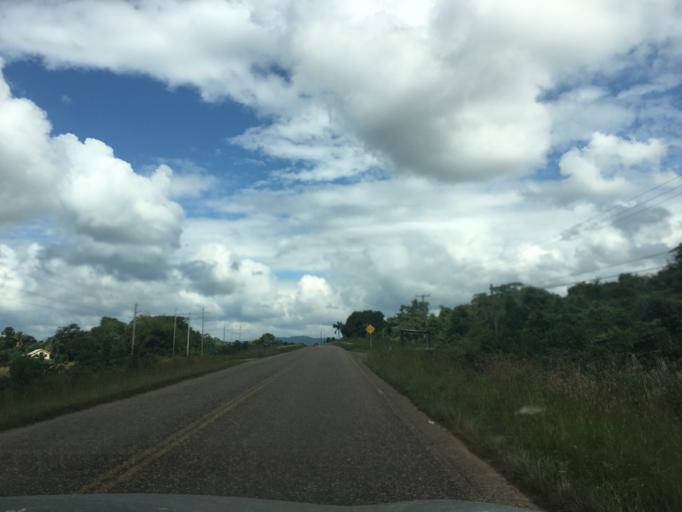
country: BZ
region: Stann Creek
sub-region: Dangriga
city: Dangriga
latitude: 16.8600
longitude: -88.3468
